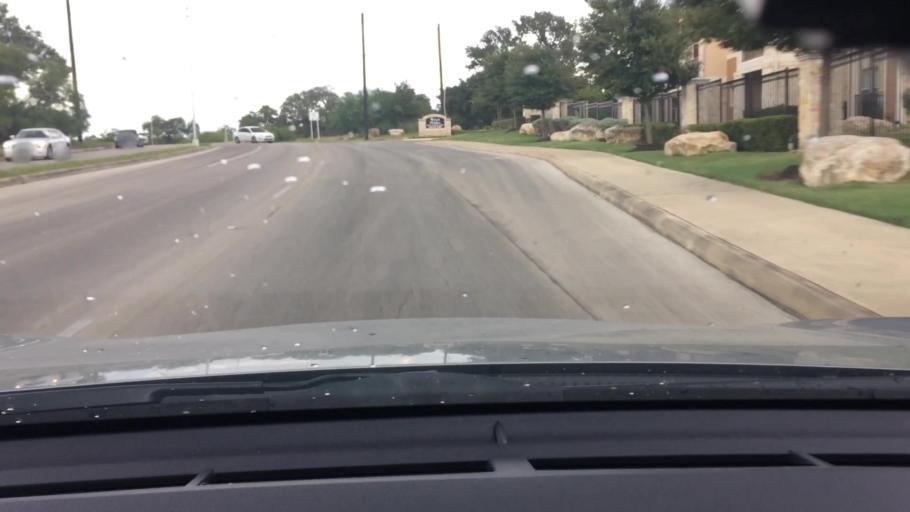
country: US
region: Texas
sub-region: Bexar County
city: Shavano Park
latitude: 29.5830
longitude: -98.5881
